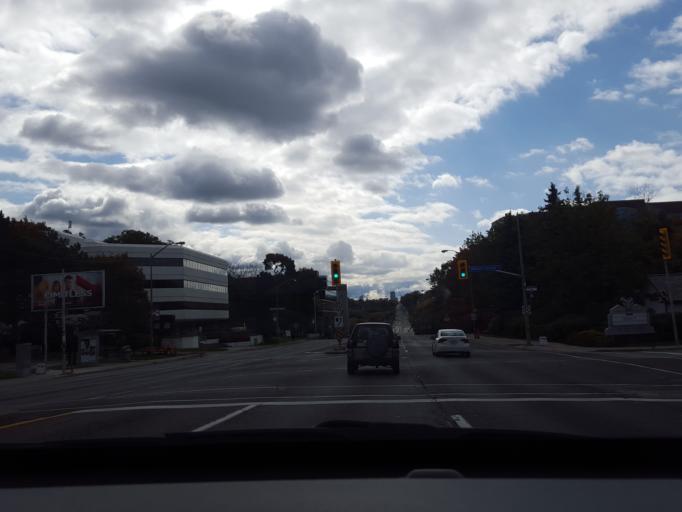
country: CA
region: Ontario
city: Willowdale
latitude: 43.7474
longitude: -79.4076
